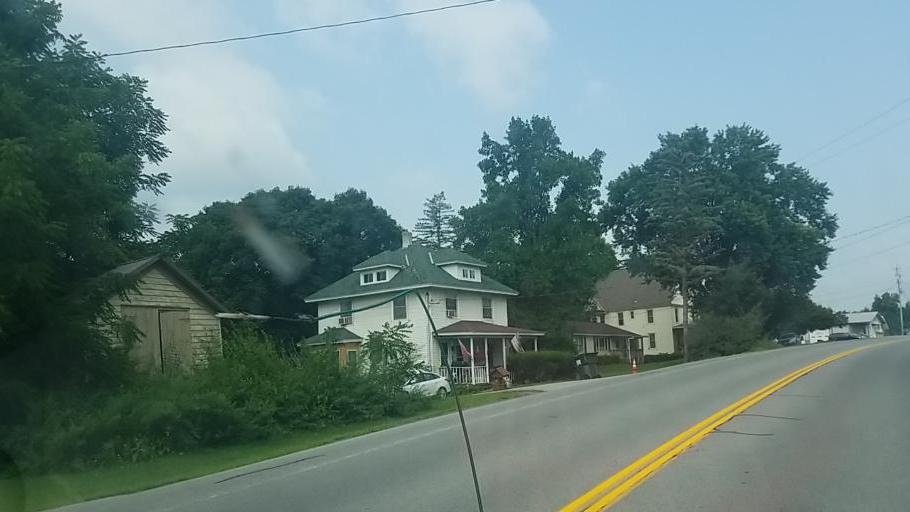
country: US
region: New York
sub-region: Montgomery County
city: Fort Plain
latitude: 42.9383
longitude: -74.6162
